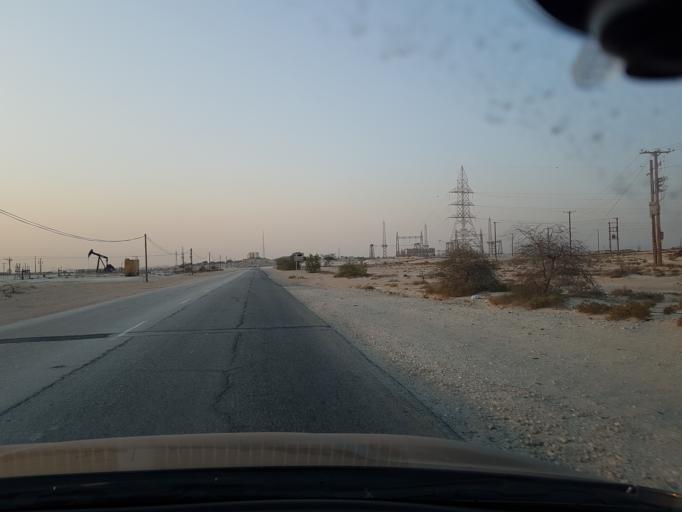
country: BH
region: Central Governorate
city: Dar Kulayb
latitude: 26.0688
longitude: 50.5527
